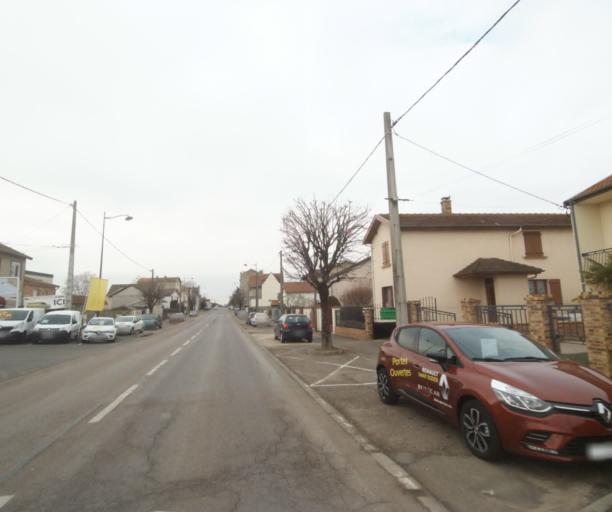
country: FR
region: Champagne-Ardenne
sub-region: Departement de la Haute-Marne
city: Bettancourt-la-Ferree
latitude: 48.6360
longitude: 4.9682
